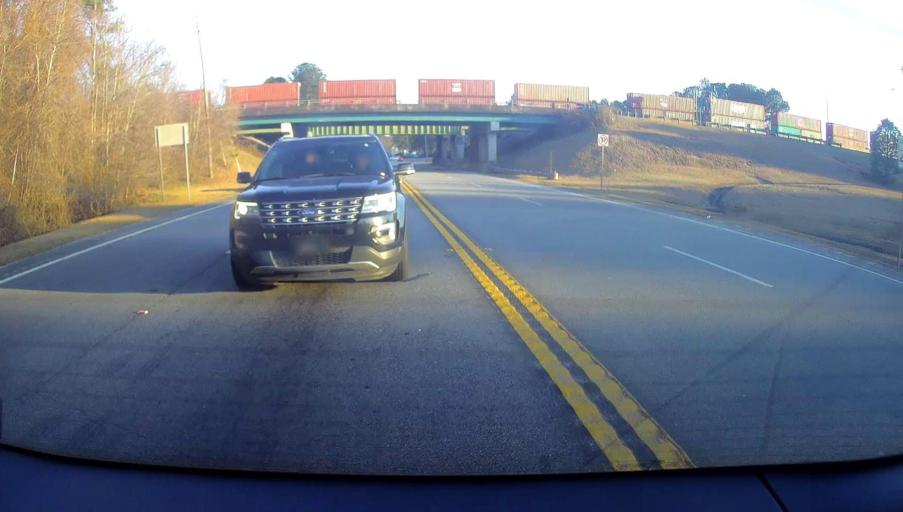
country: US
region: Georgia
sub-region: Fulton County
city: Fairburn
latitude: 33.5580
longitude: -84.5924
